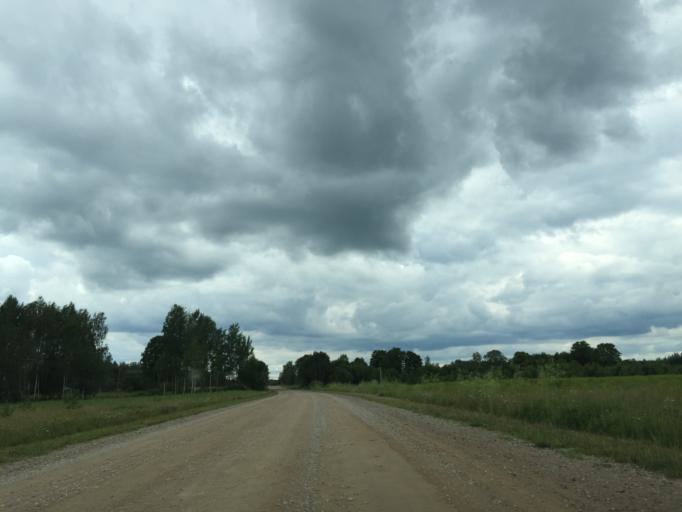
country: LV
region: Malpils
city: Malpils
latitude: 56.8802
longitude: 24.9895
